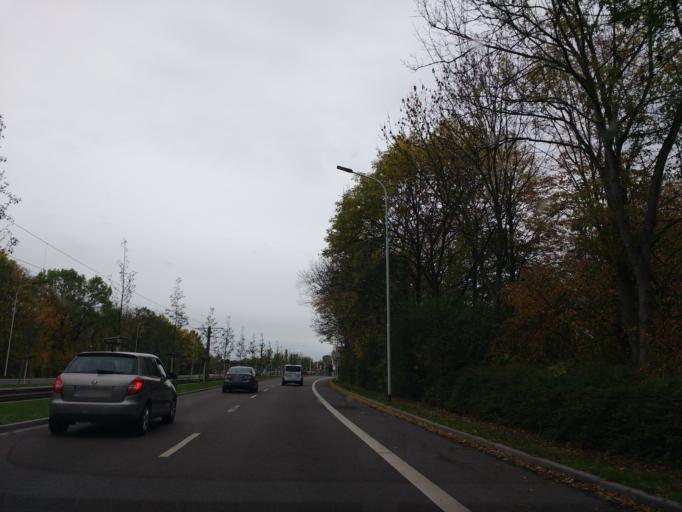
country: DE
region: Saxony-Anhalt
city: Halle Neustadt
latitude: 51.4852
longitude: 11.9463
